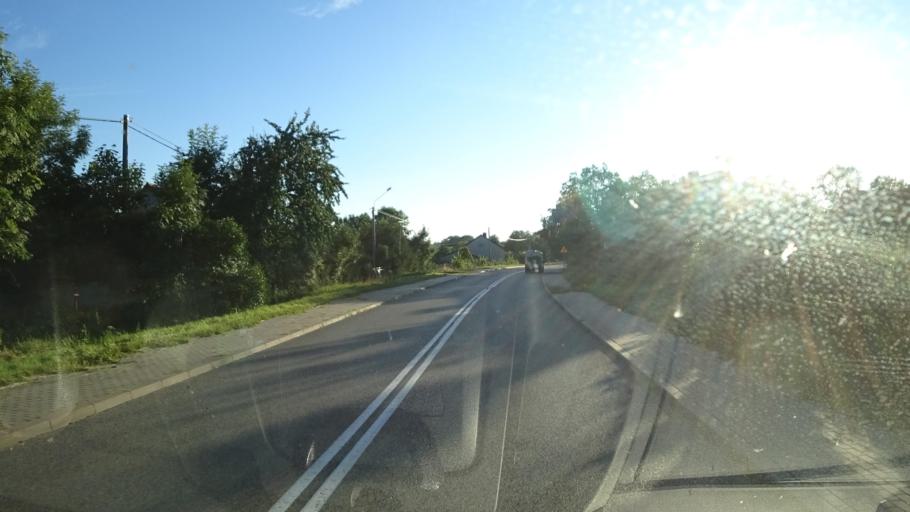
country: PL
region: Warmian-Masurian Voivodeship
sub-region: Powiat olecki
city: Olecko
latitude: 53.8604
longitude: 22.5382
